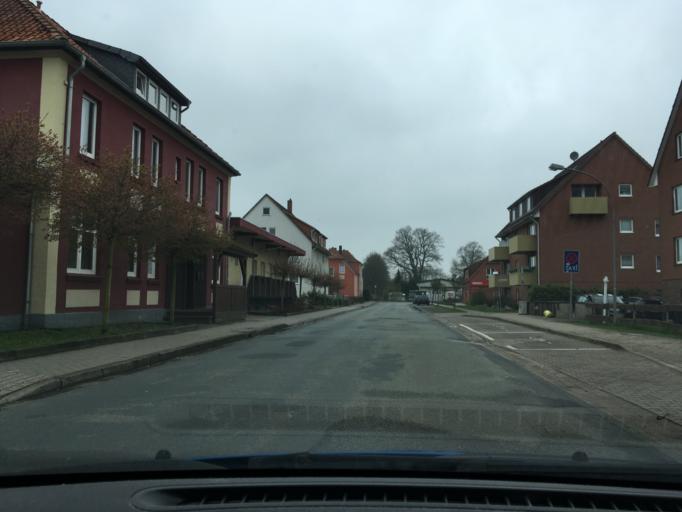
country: DE
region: Lower Saxony
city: Bleckede
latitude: 53.2917
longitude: 10.7279
